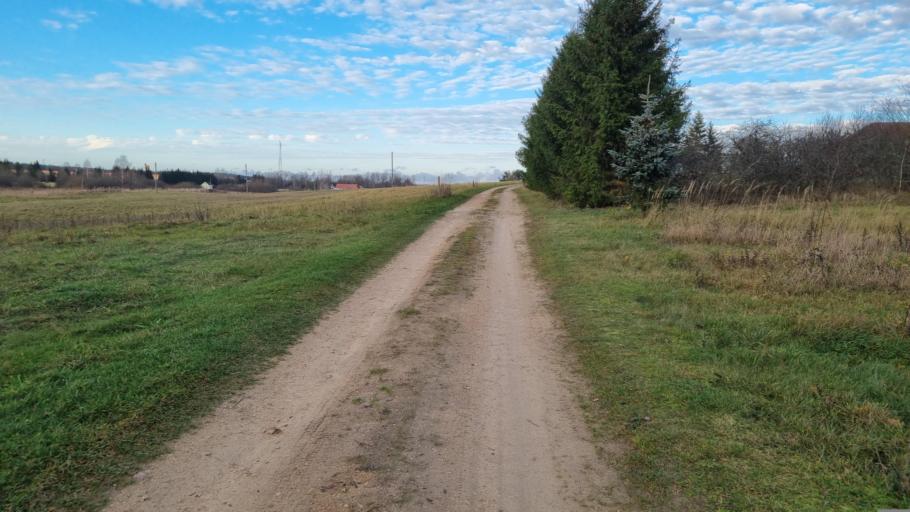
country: LV
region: Kekava
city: Kekava
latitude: 56.7860
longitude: 24.2481
